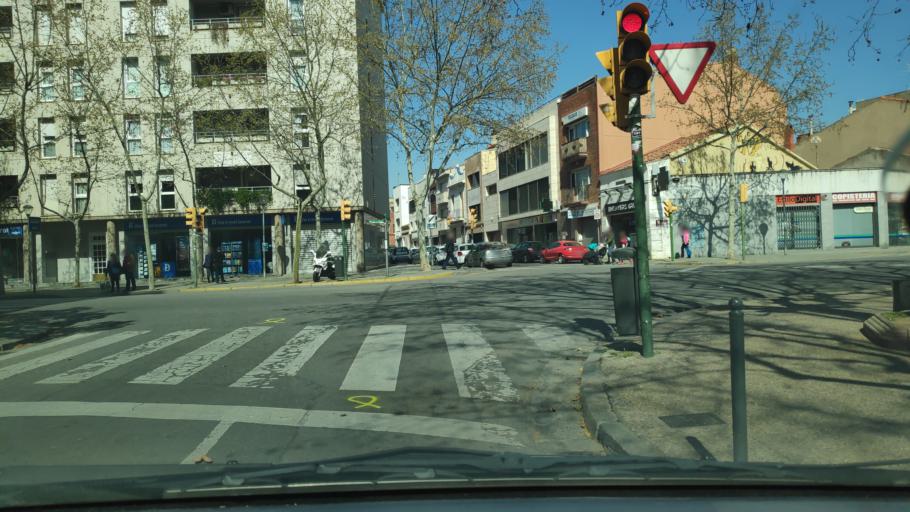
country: ES
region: Catalonia
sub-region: Provincia de Barcelona
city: Sabadell
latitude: 41.5512
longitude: 2.1037
